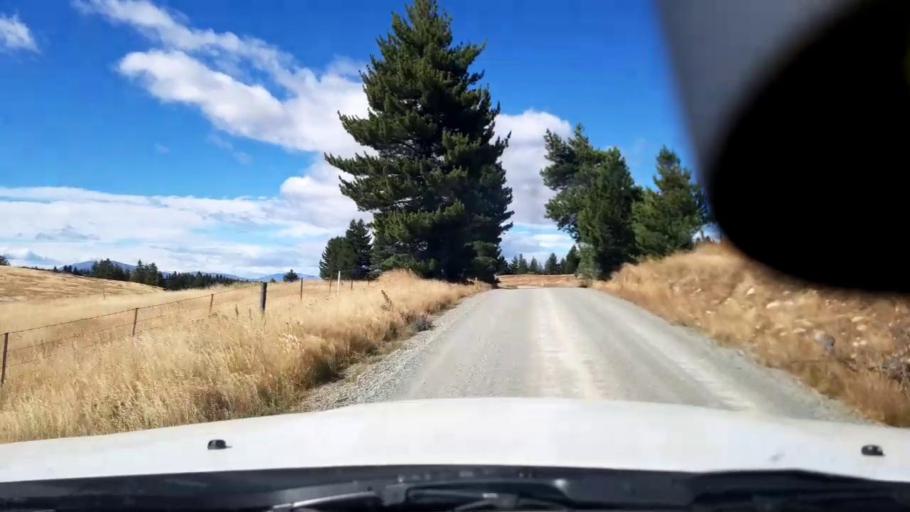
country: NZ
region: Canterbury
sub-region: Timaru District
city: Pleasant Point
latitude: -44.0094
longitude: 170.4730
